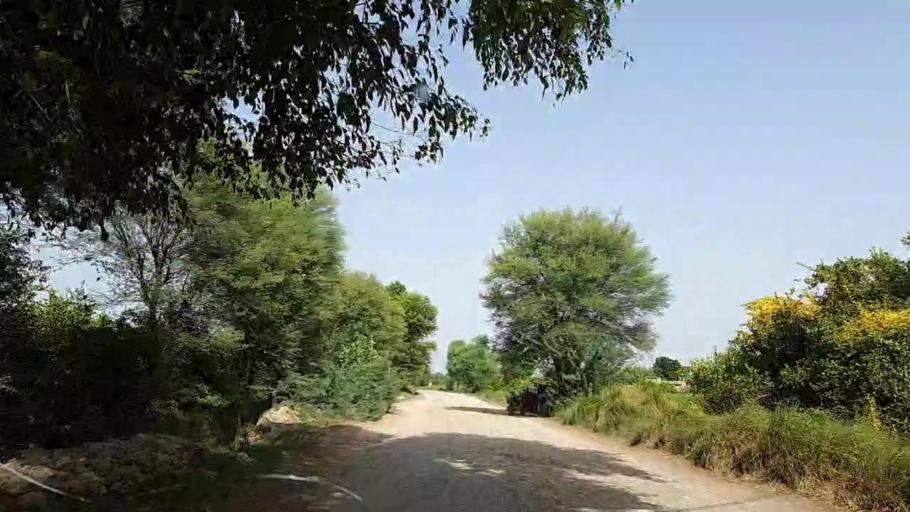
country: PK
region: Sindh
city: Kandiaro
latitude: 27.0654
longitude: 68.1846
